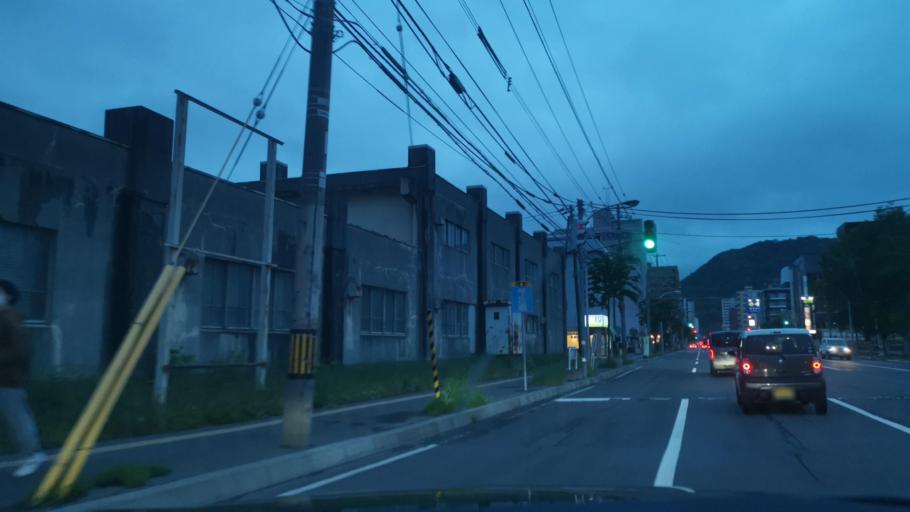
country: JP
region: Hokkaido
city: Sapporo
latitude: 43.0618
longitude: 141.3145
